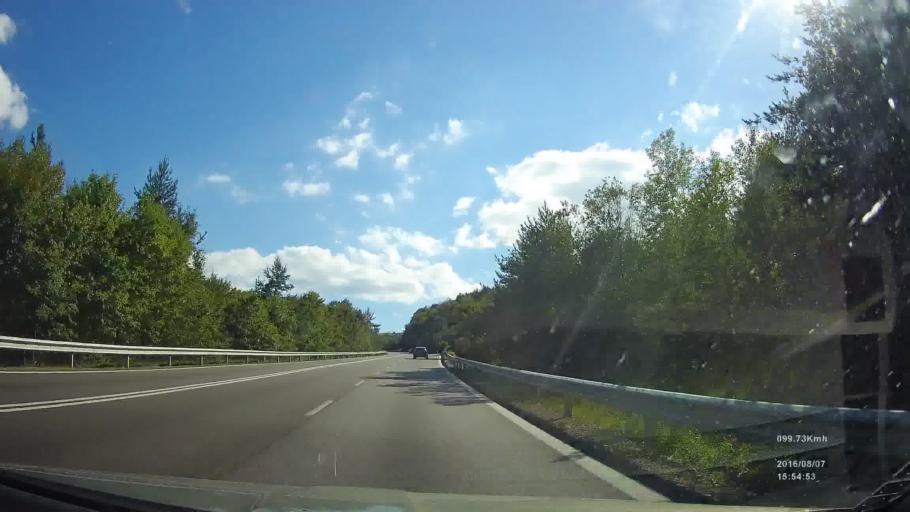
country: SK
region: Presovsky
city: Giraltovce
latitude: 49.0814
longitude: 21.4431
